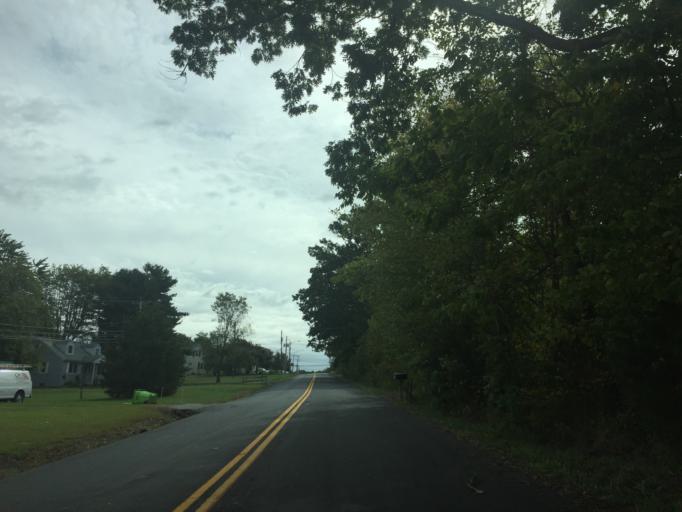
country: US
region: Maryland
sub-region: Harford County
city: Joppatowne
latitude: 39.4395
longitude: -76.3491
